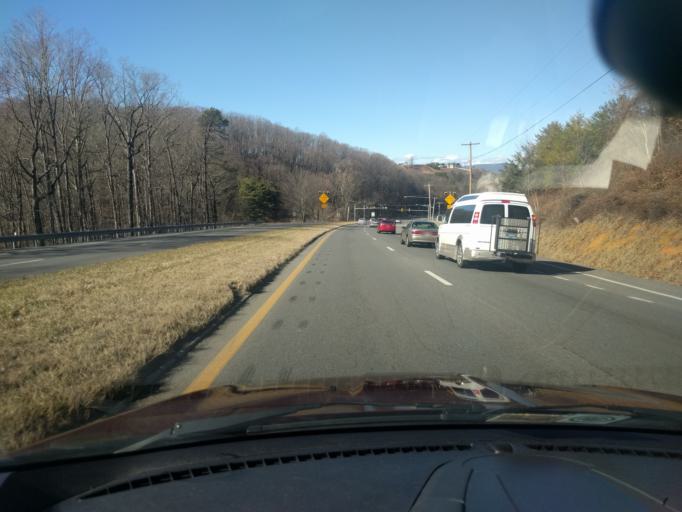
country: US
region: Virginia
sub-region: Roanoke County
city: Narrows
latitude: 37.2183
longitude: -79.9645
